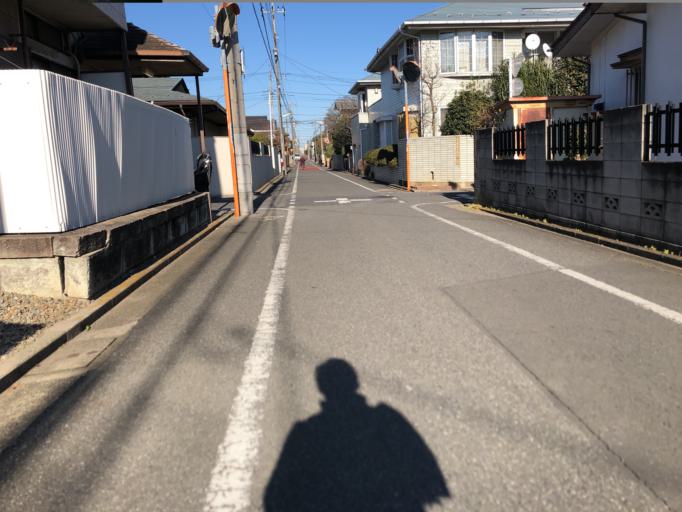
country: JP
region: Tokyo
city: Musashino
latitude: 35.7049
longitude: 139.5568
